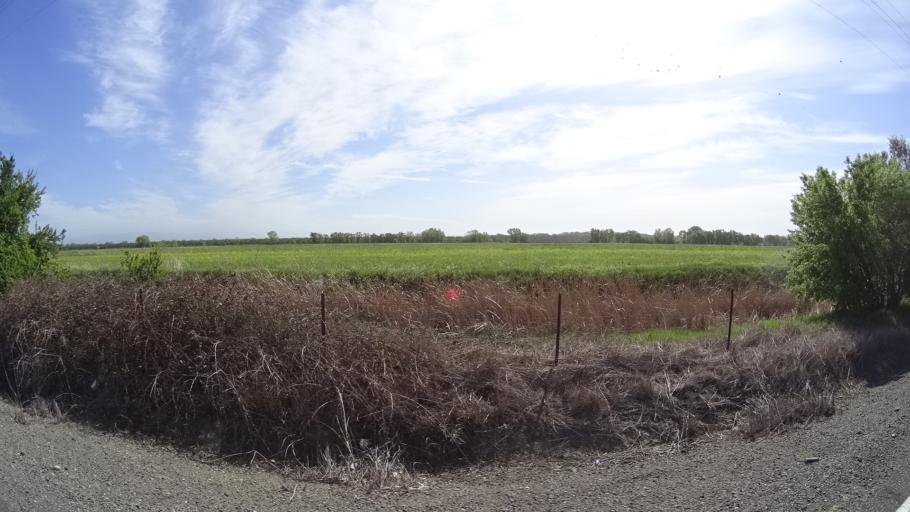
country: US
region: California
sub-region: Glenn County
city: Hamilton City
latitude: 39.6788
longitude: -122.0053
